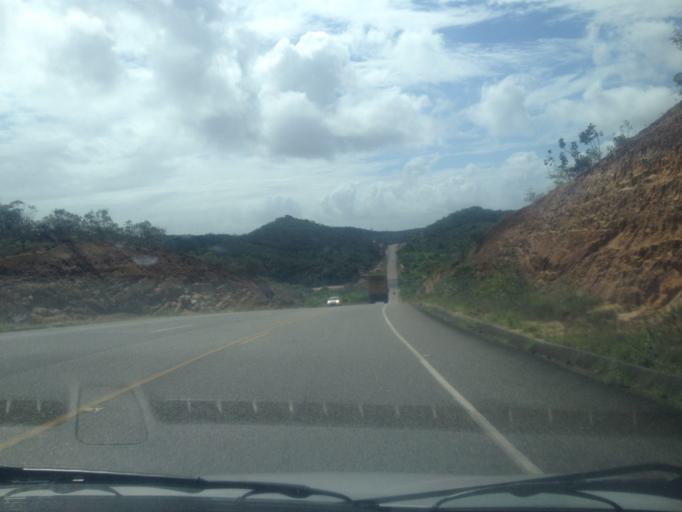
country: BR
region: Bahia
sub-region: Conde
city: Conde
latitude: -11.7320
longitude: -37.5805
